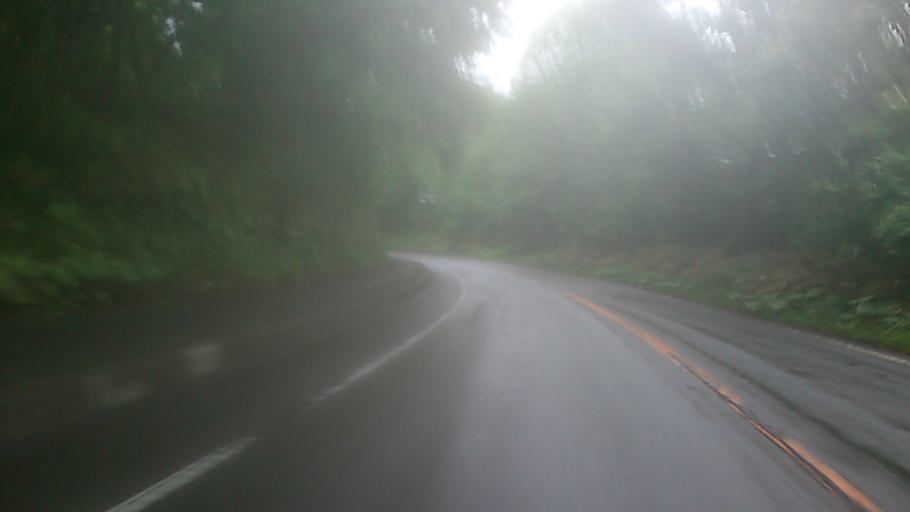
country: JP
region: Hokkaido
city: Shiraoi
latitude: 42.7709
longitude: 141.4116
